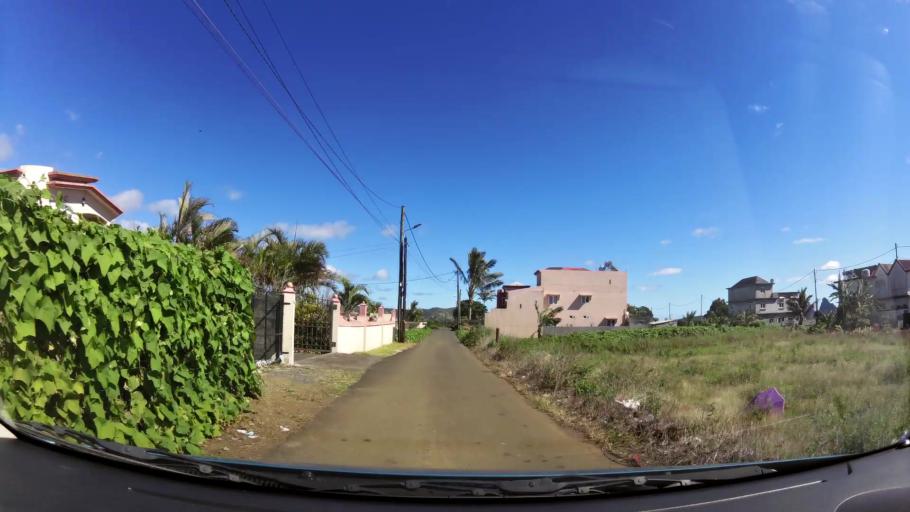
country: MU
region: Plaines Wilhems
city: Curepipe
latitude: -20.3331
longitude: 57.4898
